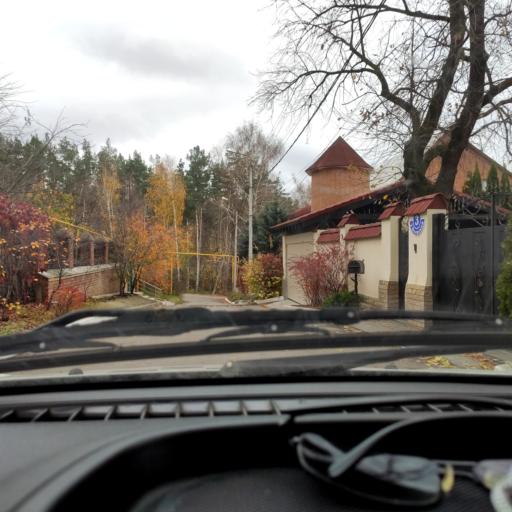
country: RU
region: Samara
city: Tol'yatti
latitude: 53.4800
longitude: 49.3554
